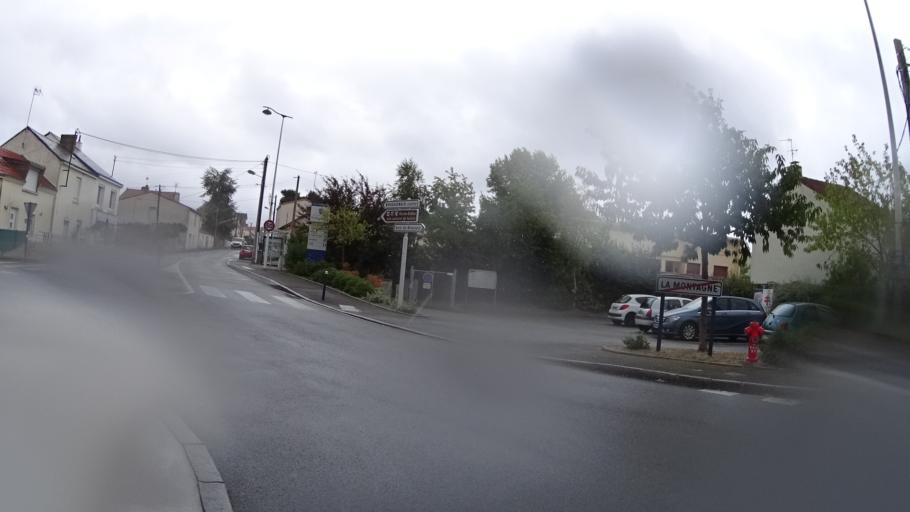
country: FR
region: Pays de la Loire
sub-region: Departement de la Loire-Atlantique
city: La Montagne
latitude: 47.1845
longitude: -1.6697
